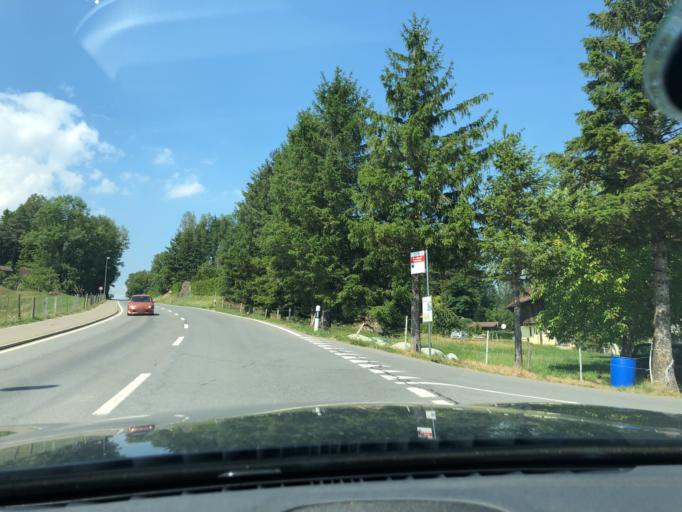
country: CH
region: Schwyz
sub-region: Bezirk Schwyz
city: Goldau
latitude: 47.0393
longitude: 8.5609
